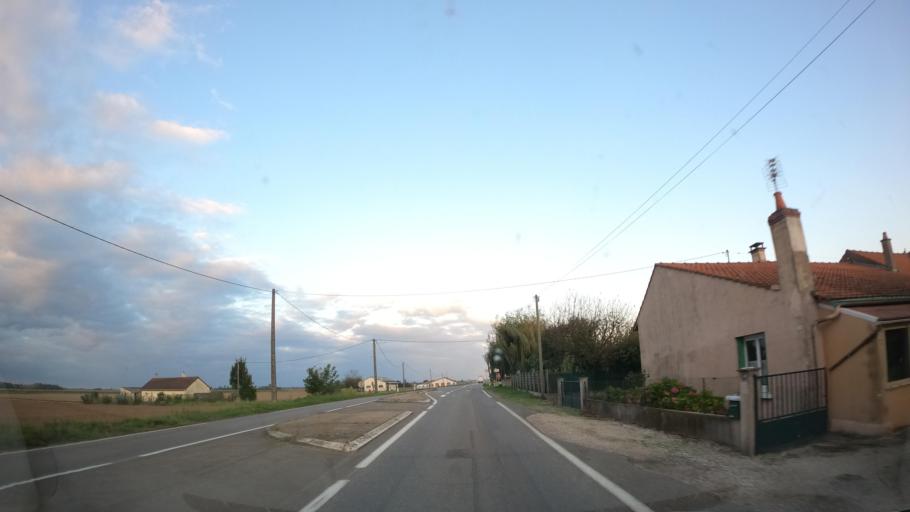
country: FR
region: Franche-Comte
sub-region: Departement du Jura
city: Petit-Noir
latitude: 46.9620
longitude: 5.2743
